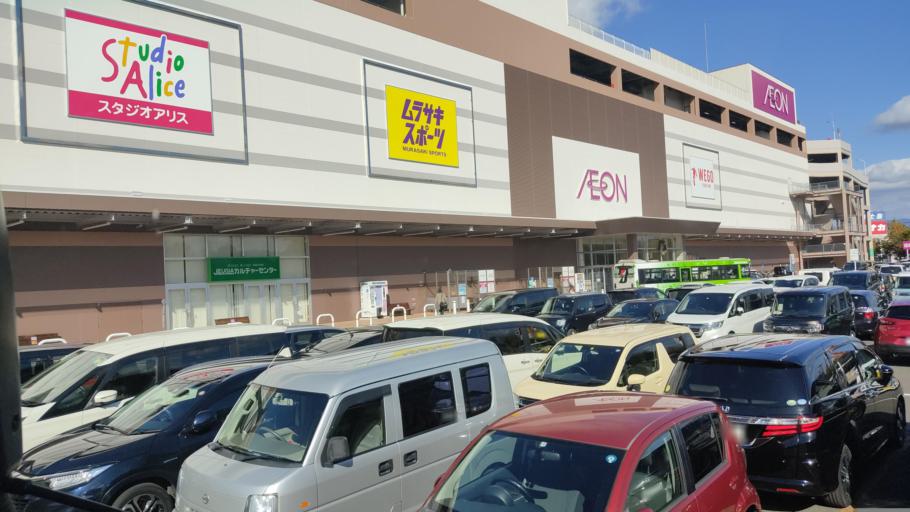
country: JP
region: Iwate
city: Morioka-shi
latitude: 39.6827
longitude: 141.1286
